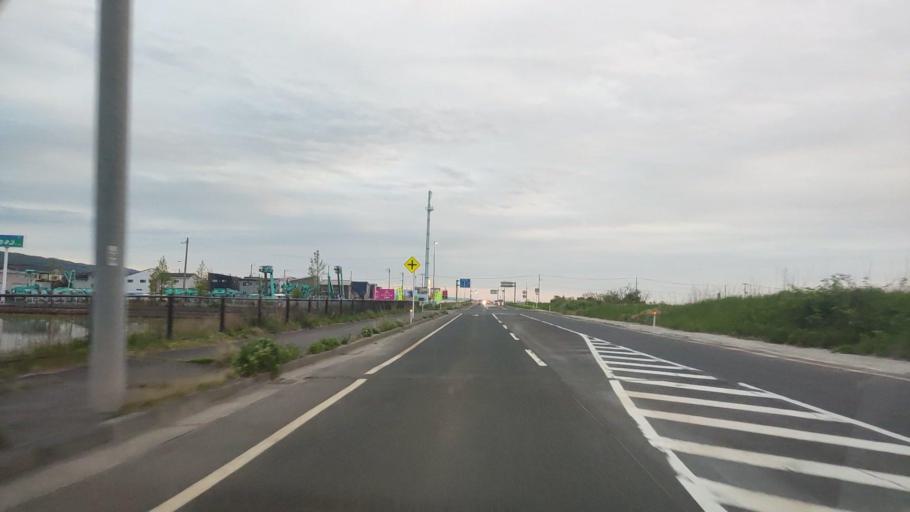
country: JP
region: Niigata
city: Niitsu-honcho
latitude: 37.7535
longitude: 139.0896
